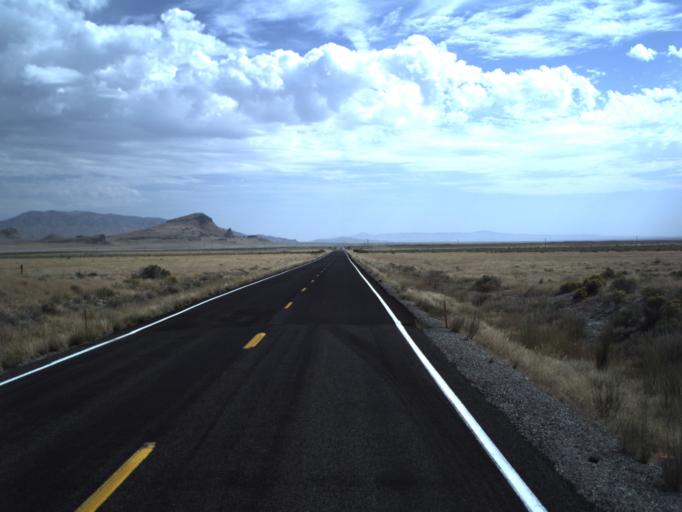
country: US
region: Utah
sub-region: Tooele County
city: Wendover
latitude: 41.4201
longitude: -113.9020
